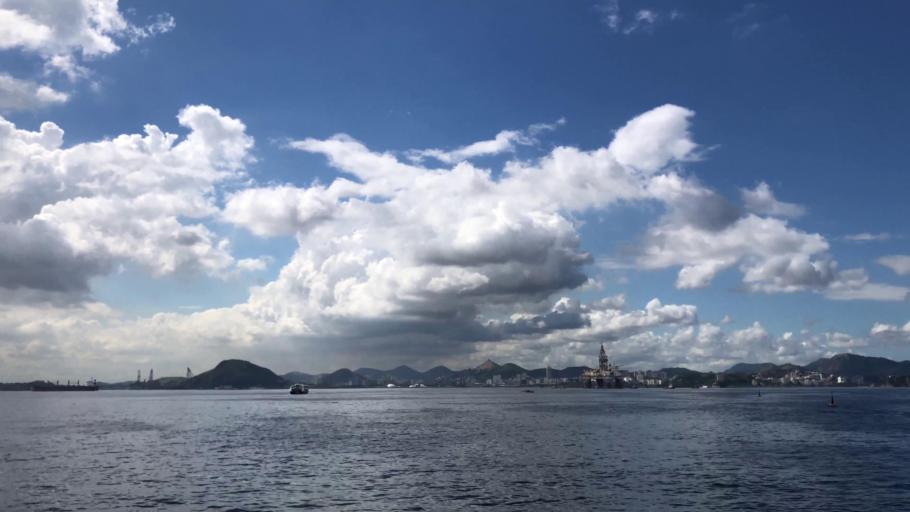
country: BR
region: Rio de Janeiro
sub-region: Rio De Janeiro
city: Rio de Janeiro
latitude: -22.9000
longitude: -43.1613
